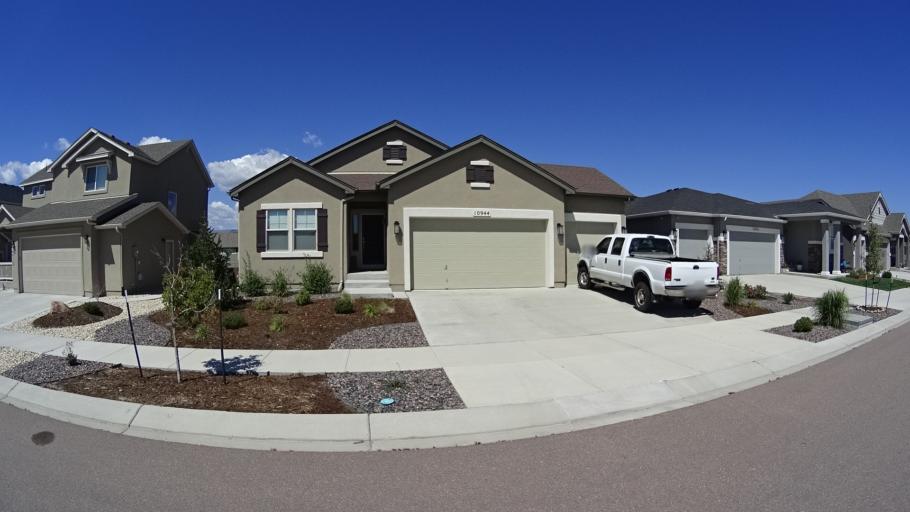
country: US
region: Colorado
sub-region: El Paso County
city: Black Forest
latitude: 38.9895
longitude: -104.7588
